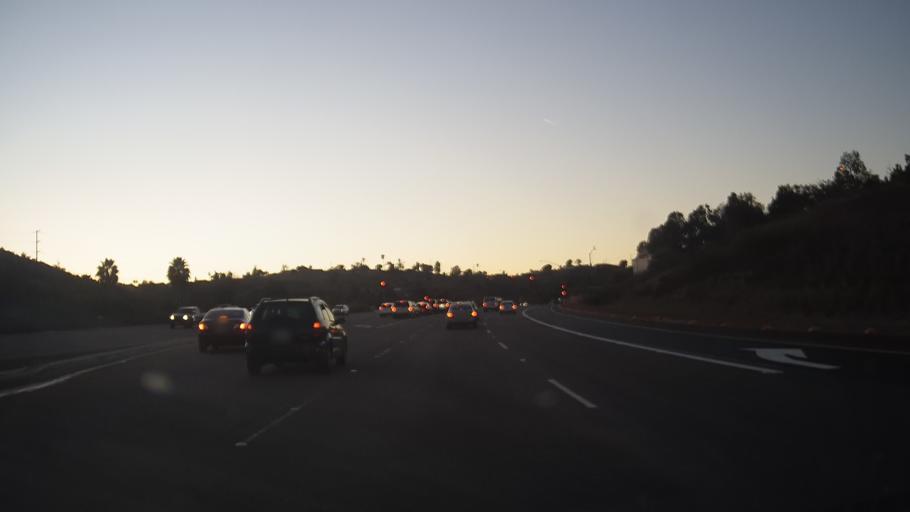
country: US
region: California
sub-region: San Diego County
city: Rancho San Diego
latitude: 32.7387
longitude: -116.9513
